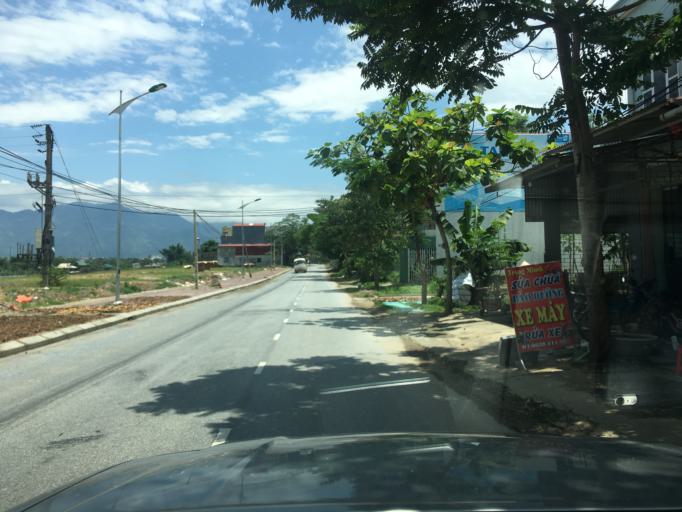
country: VN
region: Yen Bai
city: Son Thinh
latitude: 21.6187
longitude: 104.5085
